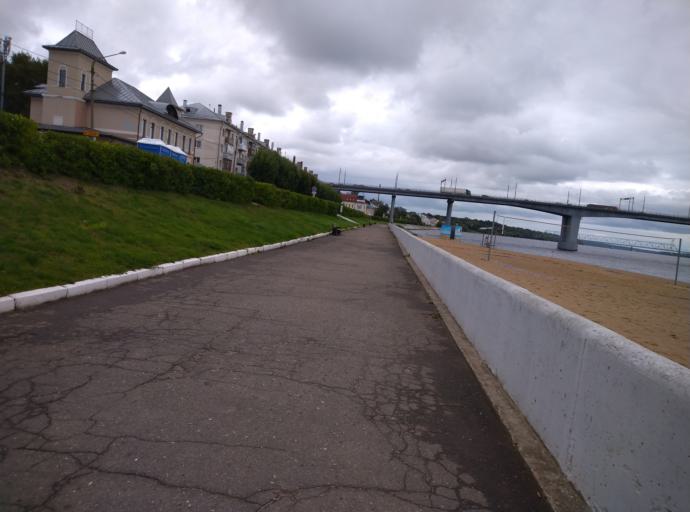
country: RU
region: Kostroma
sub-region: Kostromskoy Rayon
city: Kostroma
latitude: 57.7575
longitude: 40.9393
